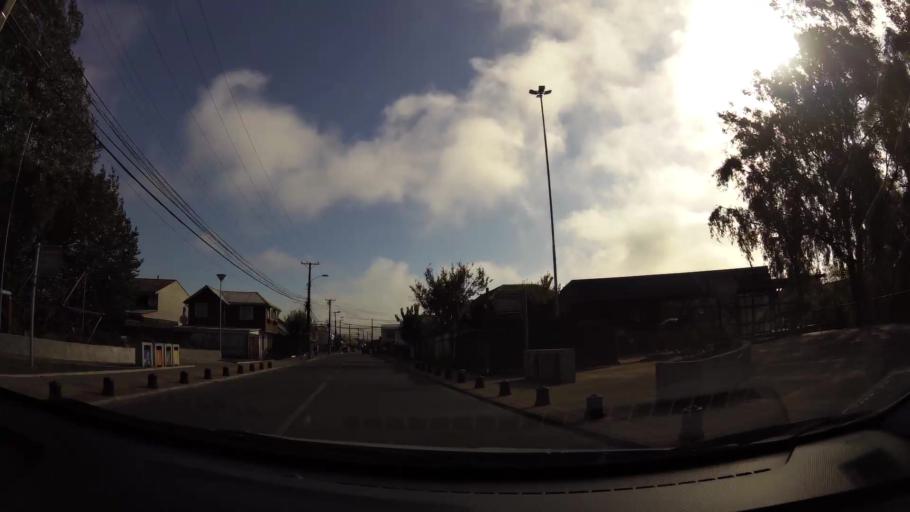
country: CL
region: Biobio
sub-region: Provincia de Concepcion
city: Concepcion
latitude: -36.7992
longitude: -73.0969
